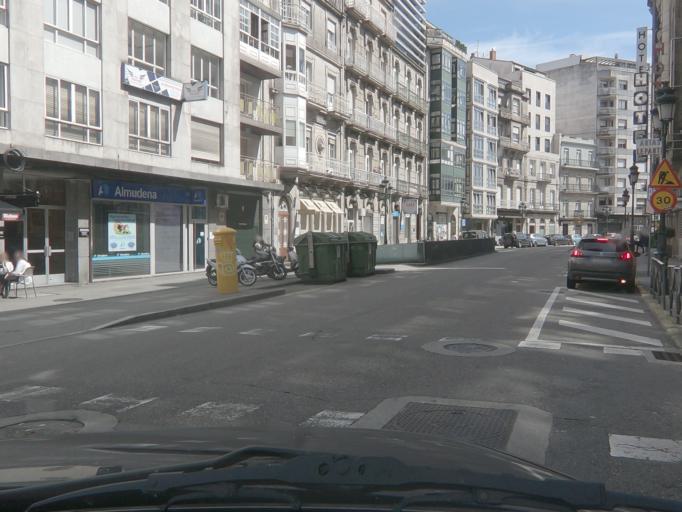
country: ES
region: Galicia
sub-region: Provincia de Pontevedra
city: Vigo
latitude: 42.2344
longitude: -8.7113
